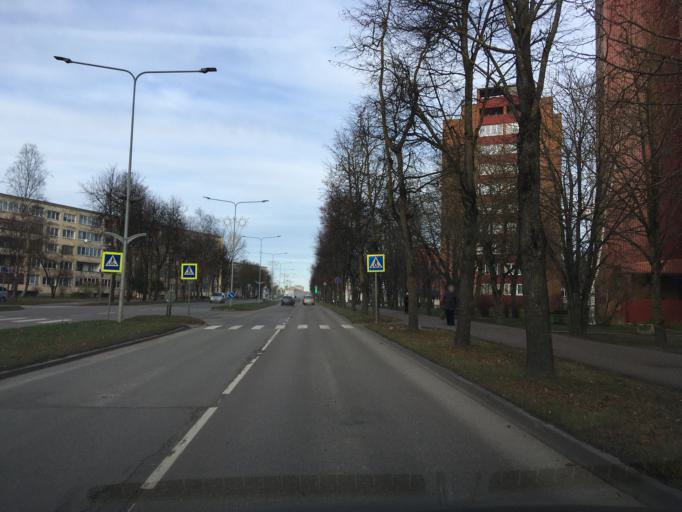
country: EE
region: Ida-Virumaa
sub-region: Narva linn
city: Narva
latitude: 59.3672
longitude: 28.1868
